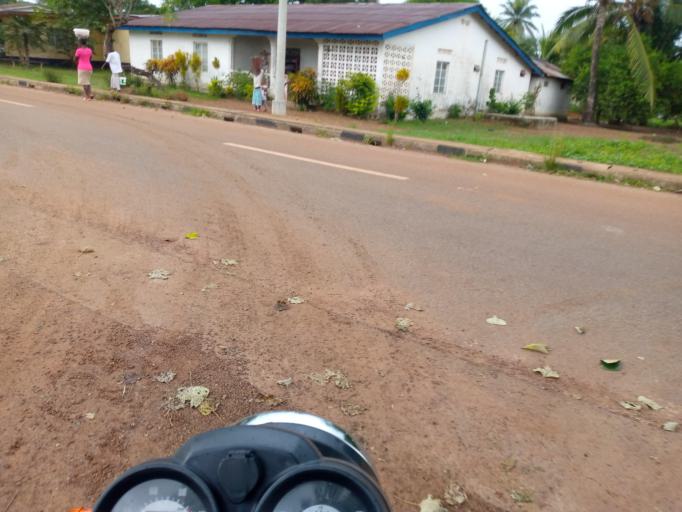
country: SL
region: Southern Province
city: Moyamba
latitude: 8.1486
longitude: -12.4366
